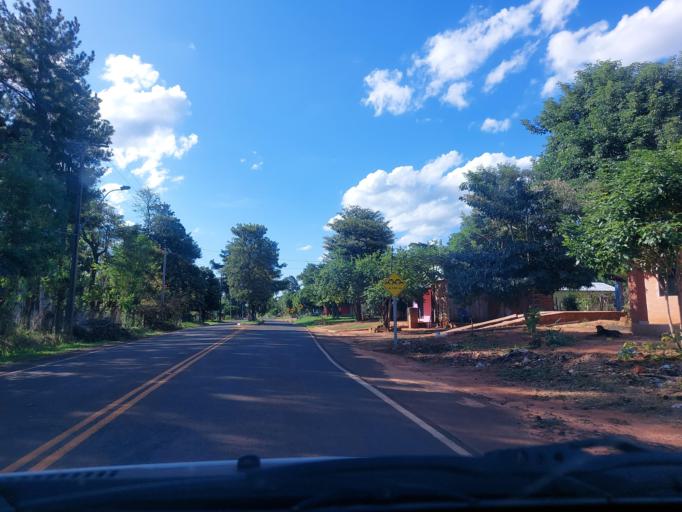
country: PY
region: San Pedro
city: Guayaybi
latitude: -24.5695
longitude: -56.5195
